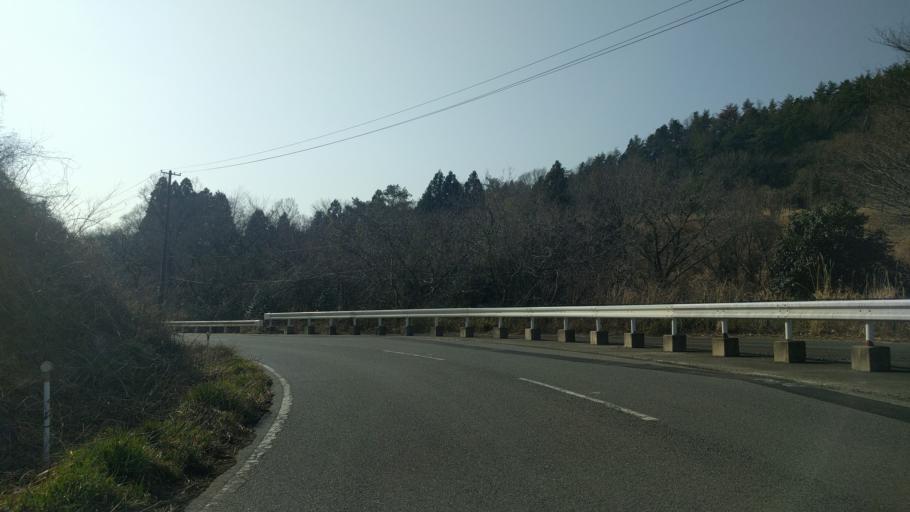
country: JP
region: Fukushima
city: Iwaki
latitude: 37.0374
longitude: 140.8097
